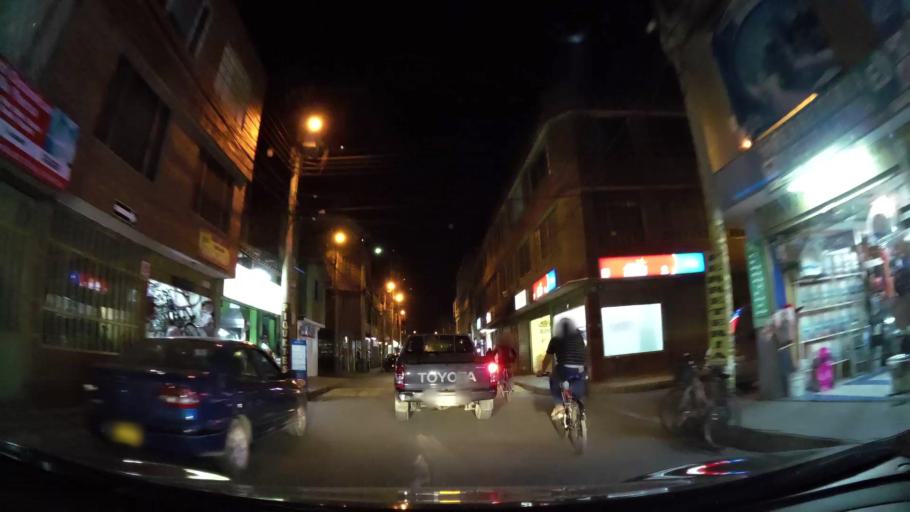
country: CO
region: Cundinamarca
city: Funza
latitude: 4.7134
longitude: -74.2201
